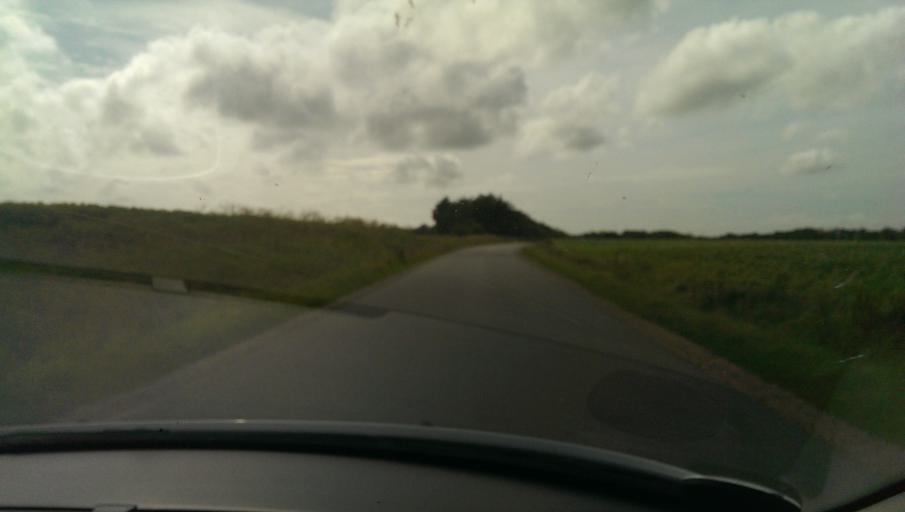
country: DK
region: Central Jutland
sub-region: Holstebro Kommune
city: Ulfborg
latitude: 56.2753
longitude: 8.2667
